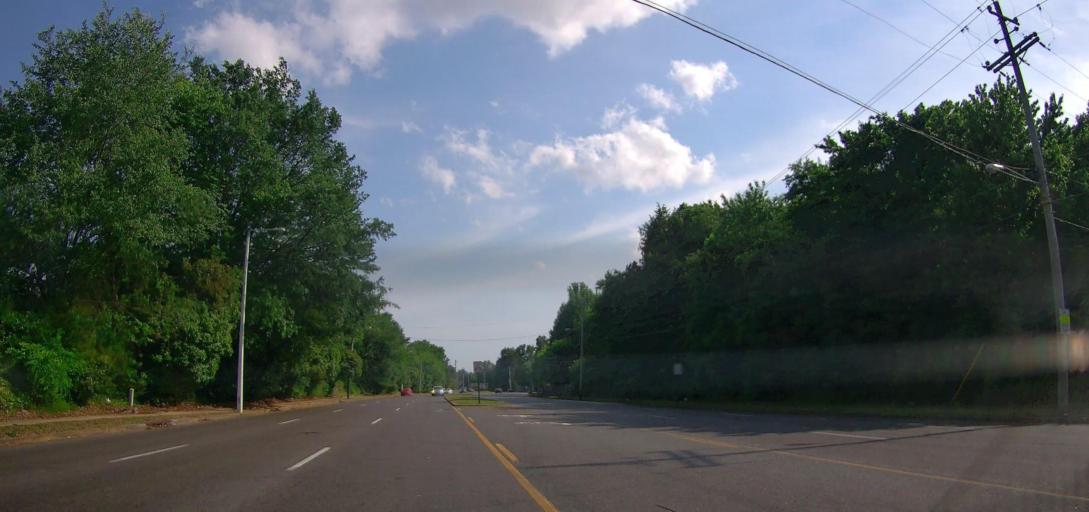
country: US
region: Tennessee
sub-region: Shelby County
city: Germantown
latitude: 35.0344
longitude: -89.8477
